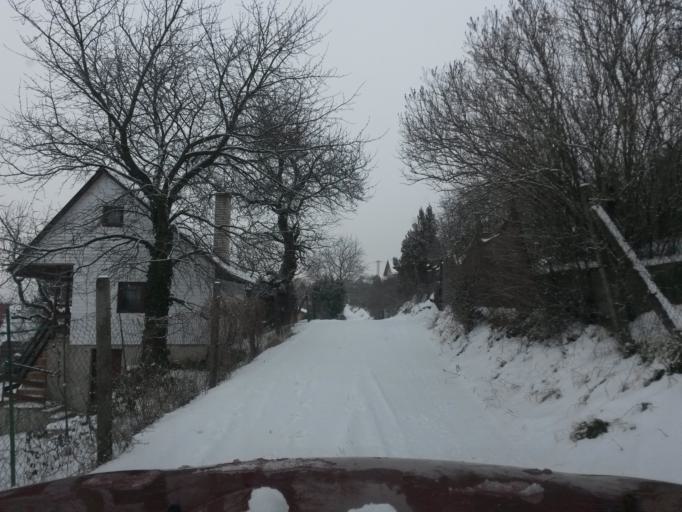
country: SK
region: Kosicky
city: Kosice
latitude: 48.7234
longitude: 21.3270
